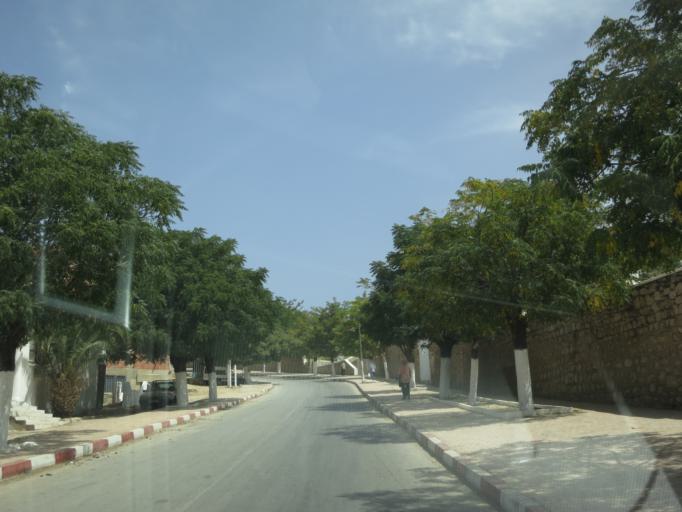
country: MA
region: Meknes-Tafilalet
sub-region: Meknes
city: Meknes
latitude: 34.0572
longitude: -5.5199
